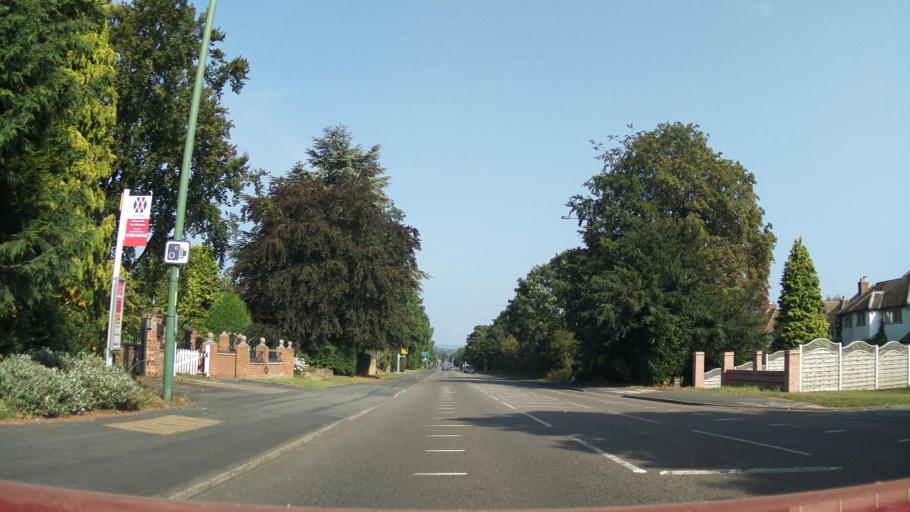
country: GB
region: England
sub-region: Walsall
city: Streetly
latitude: 52.5806
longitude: -1.8855
